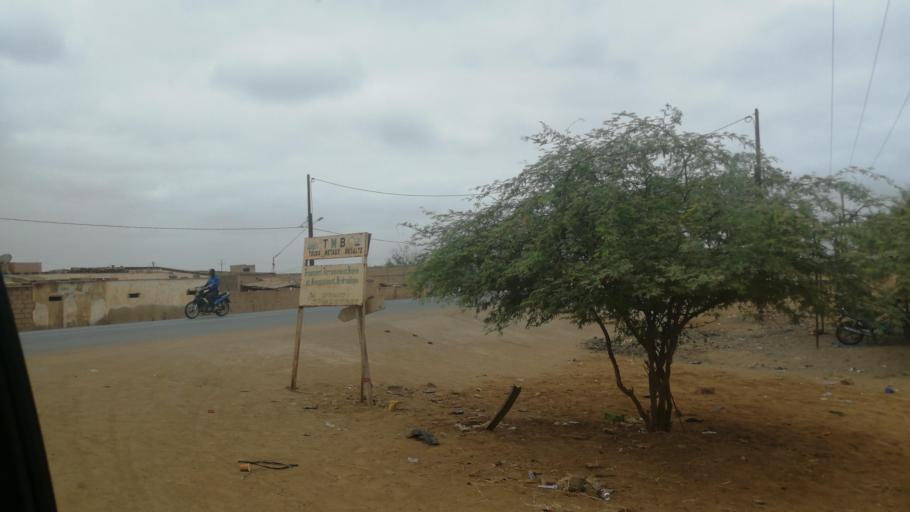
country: SN
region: Saint-Louis
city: Rosso
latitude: 16.2766
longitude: -16.1475
